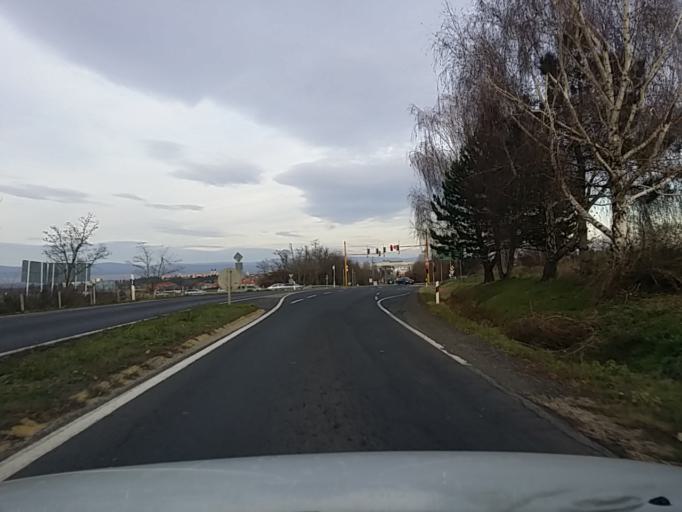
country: HU
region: Veszprem
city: Veszprem
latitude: 47.0783
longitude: 17.8922
